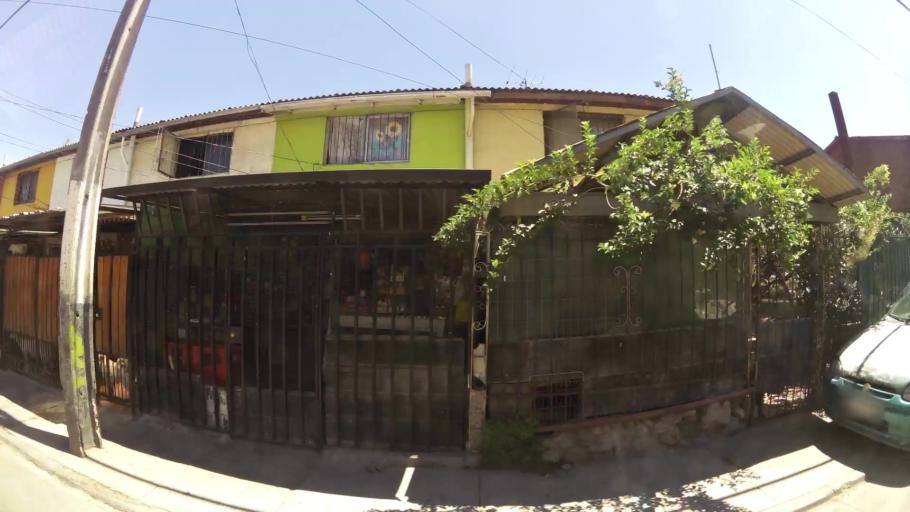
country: CL
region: Santiago Metropolitan
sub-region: Provincia de Maipo
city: San Bernardo
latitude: -33.5831
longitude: -70.6693
